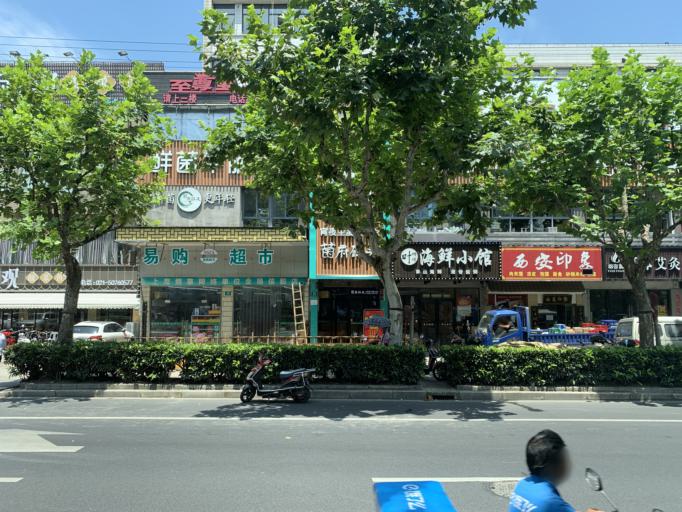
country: CN
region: Shanghai Shi
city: Pudong
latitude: 31.2485
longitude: 121.5671
